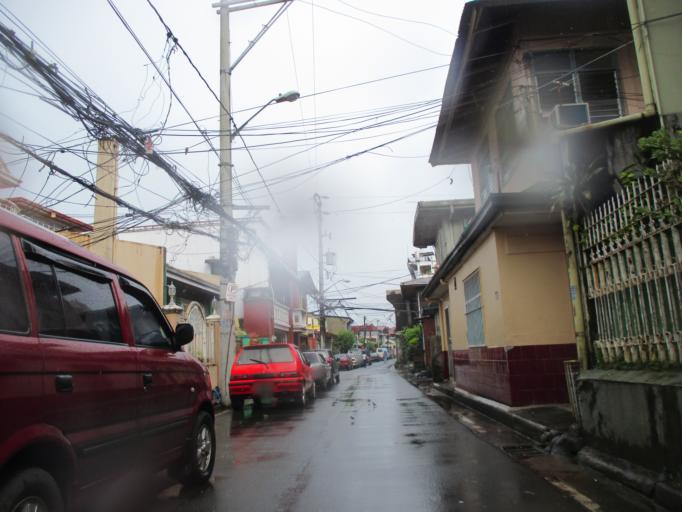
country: PH
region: Metro Manila
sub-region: Marikina
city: Calumpang
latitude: 14.6306
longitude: 121.0955
